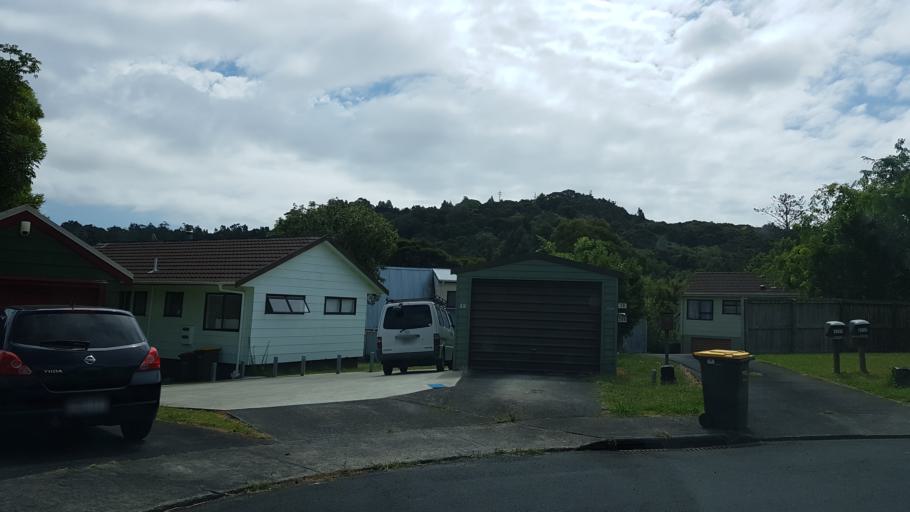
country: NZ
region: Auckland
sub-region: Auckland
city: North Shore
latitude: -36.7767
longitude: 174.7007
